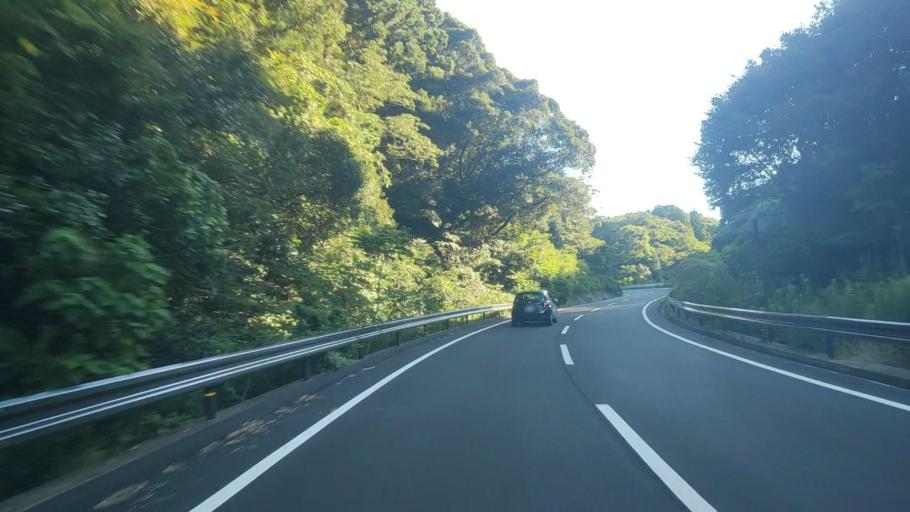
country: JP
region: Mie
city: Toba
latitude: 34.3066
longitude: 136.8795
